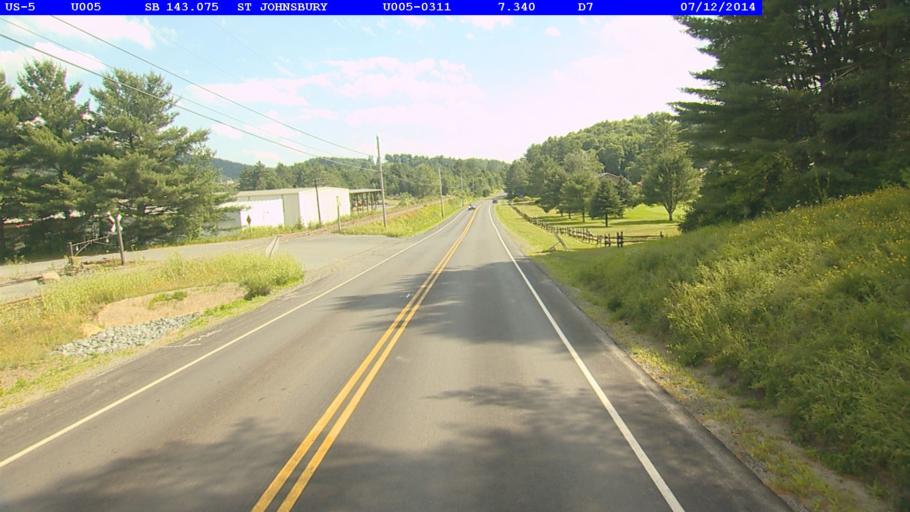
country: US
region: Vermont
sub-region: Caledonia County
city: Lyndon
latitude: 44.4938
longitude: -72.0049
